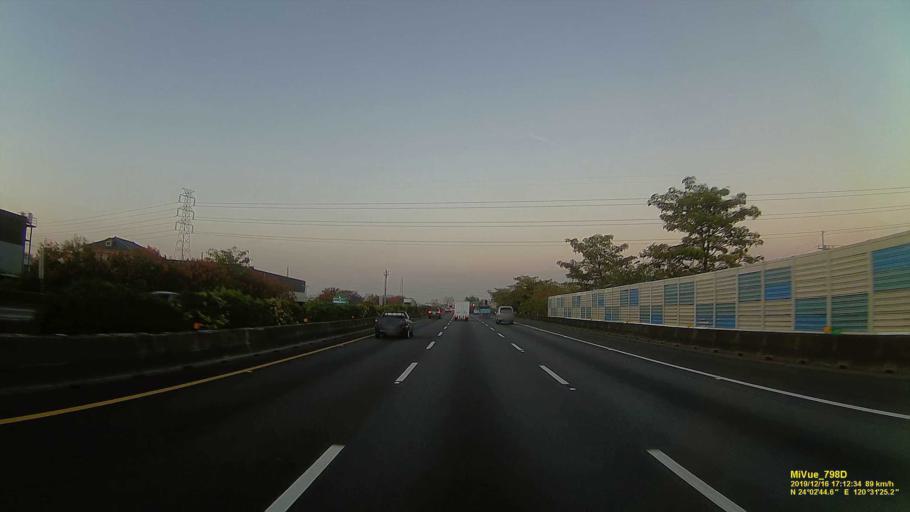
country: TW
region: Taiwan
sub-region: Changhua
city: Chang-hua
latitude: 24.0462
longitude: 120.5237
